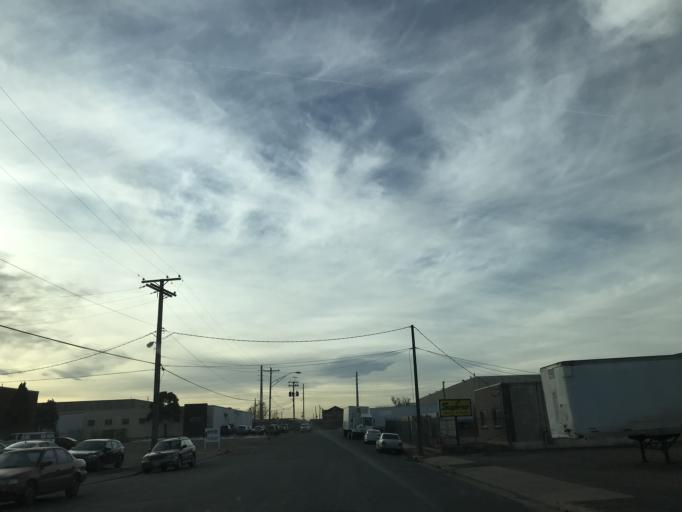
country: US
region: Colorado
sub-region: Adams County
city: Commerce City
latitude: 39.7781
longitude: -104.9247
